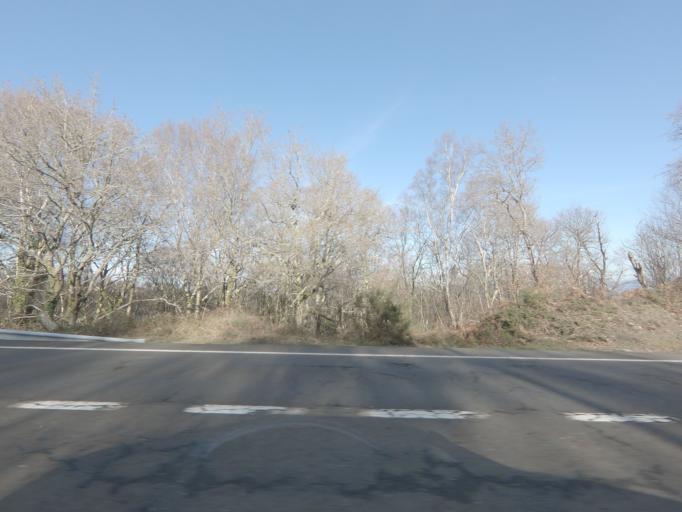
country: ES
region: Galicia
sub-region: Provincia de Pontevedra
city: Silleda
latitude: 42.7034
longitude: -8.3423
